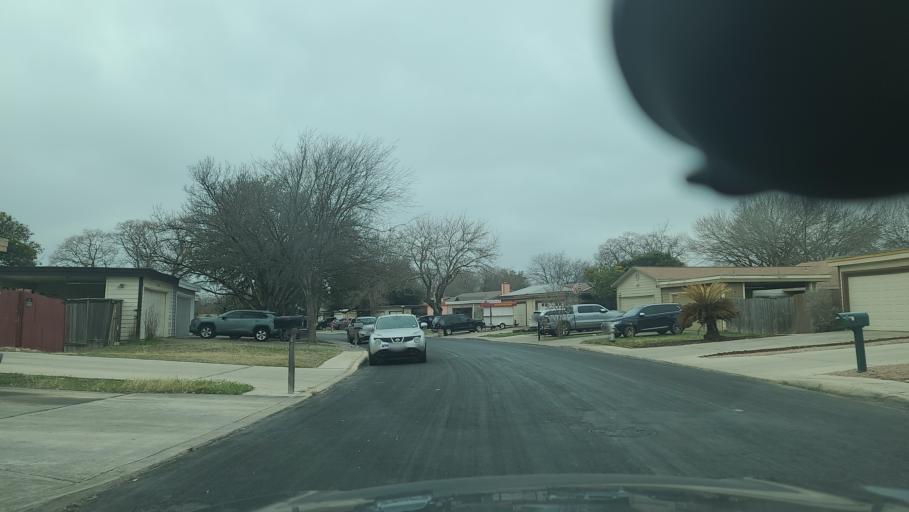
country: US
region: Texas
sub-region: Bexar County
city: Leon Valley
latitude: 29.5553
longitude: -98.6243
